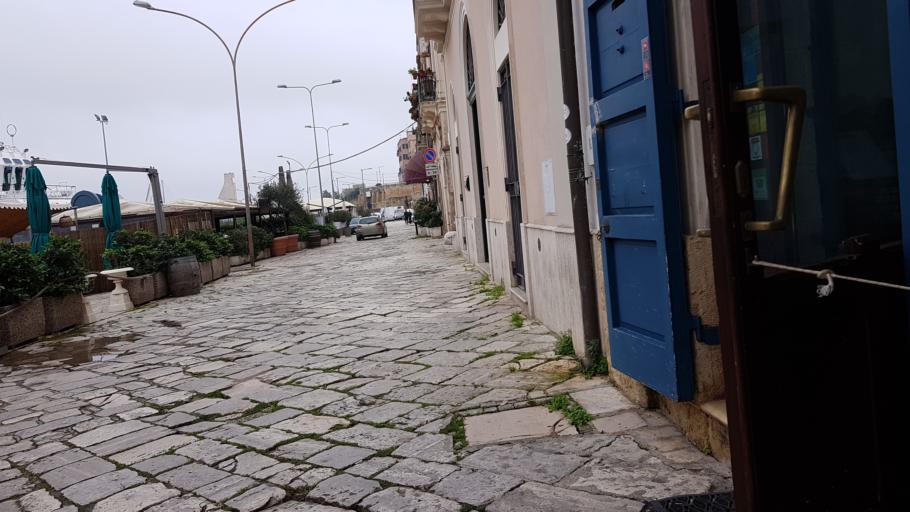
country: IT
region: Apulia
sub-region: Provincia di Brindisi
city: Brindisi
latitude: 40.6403
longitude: 17.9408
